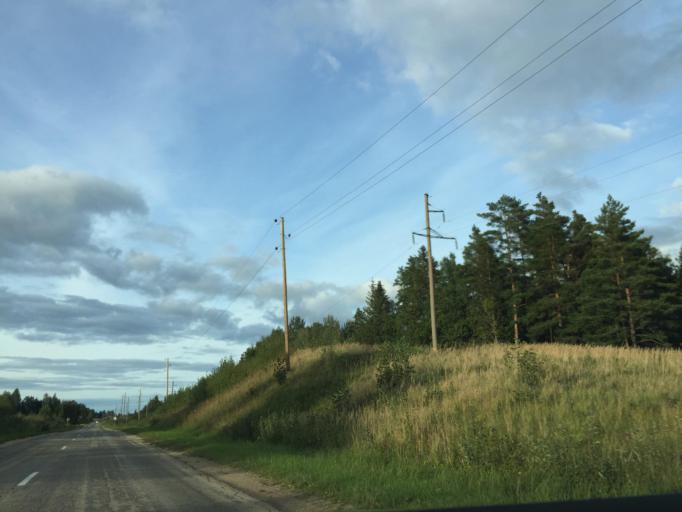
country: LV
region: Nereta
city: Nereta
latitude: 56.2359
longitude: 25.3263
